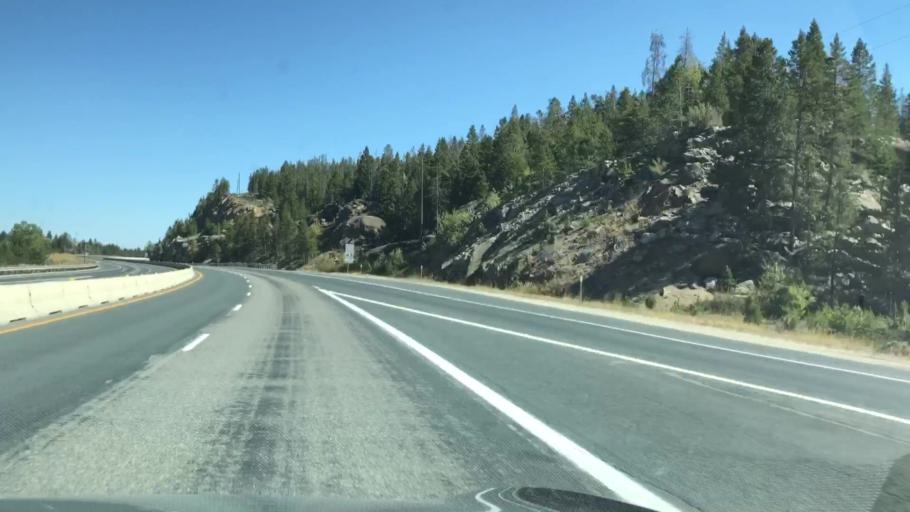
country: US
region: Montana
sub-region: Silver Bow County
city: Butte
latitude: 45.9157
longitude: -112.3742
